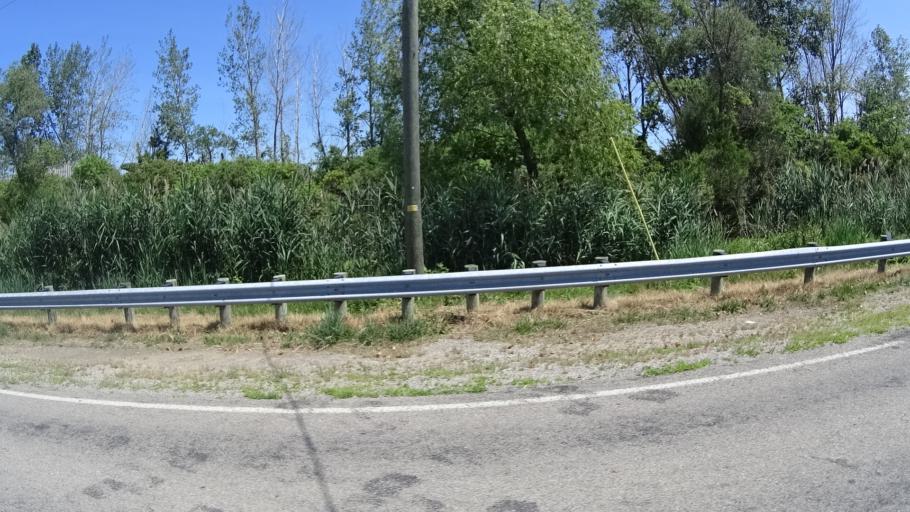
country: US
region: Ohio
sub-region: Erie County
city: Sandusky
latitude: 41.4634
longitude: -82.8003
